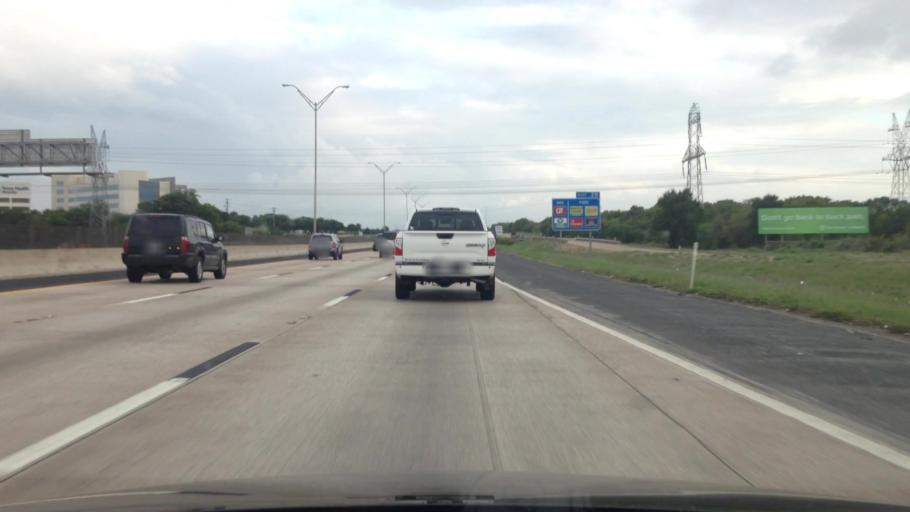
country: US
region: Texas
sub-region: Tarrant County
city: Crowley
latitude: 32.5915
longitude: -97.3196
